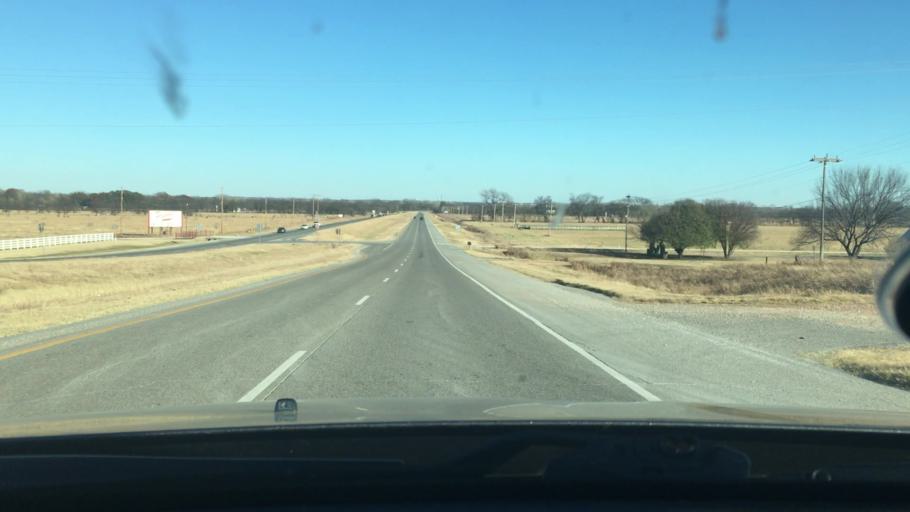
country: US
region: Oklahoma
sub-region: Murray County
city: Davis
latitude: 34.5064
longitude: -97.1707
